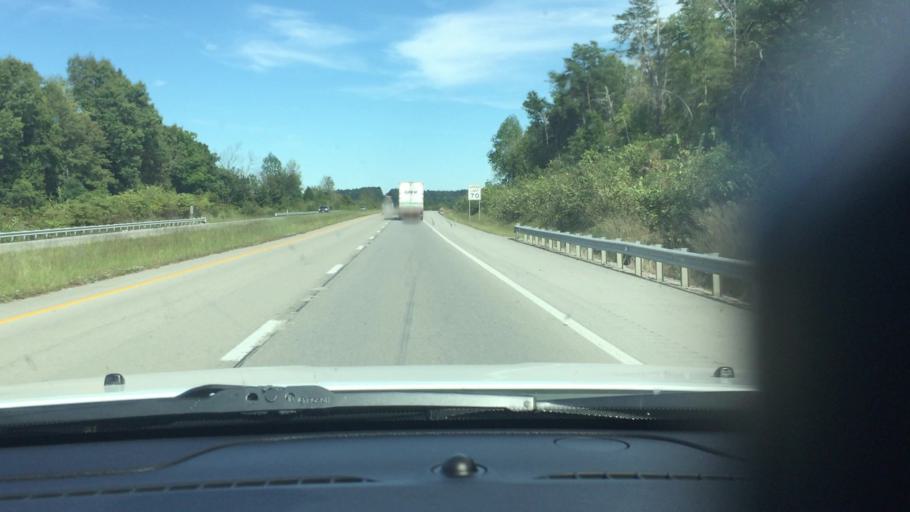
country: US
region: Kentucky
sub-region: Caldwell County
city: Princeton
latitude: 37.1368
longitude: -87.8590
